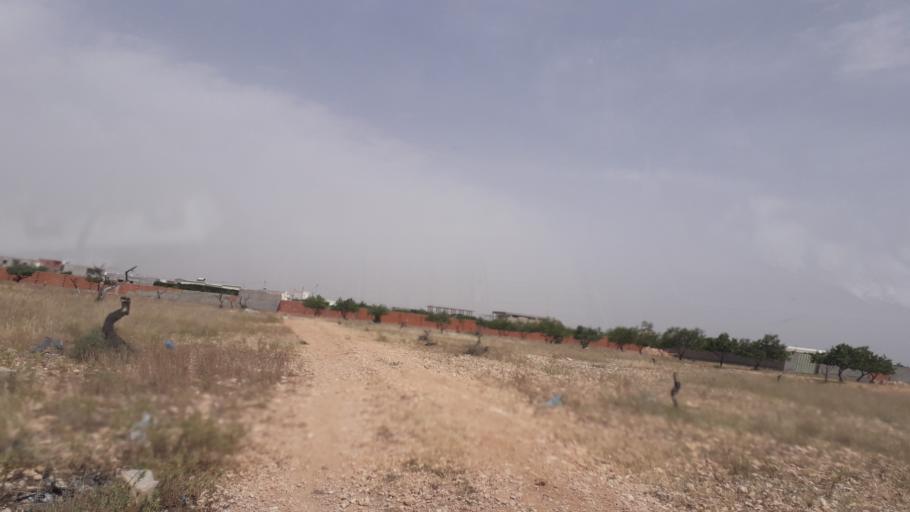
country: TN
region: Safaqis
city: Al Qarmadah
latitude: 34.8398
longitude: 10.7799
